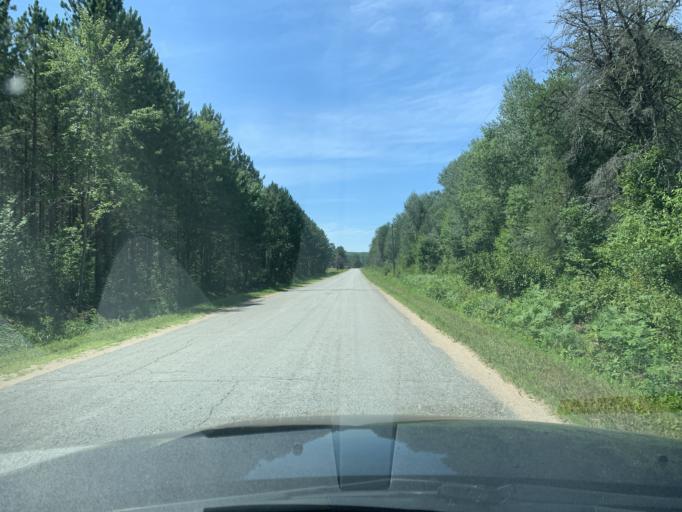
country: CA
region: Ontario
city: Petawawa
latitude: 45.6595
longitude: -77.5971
